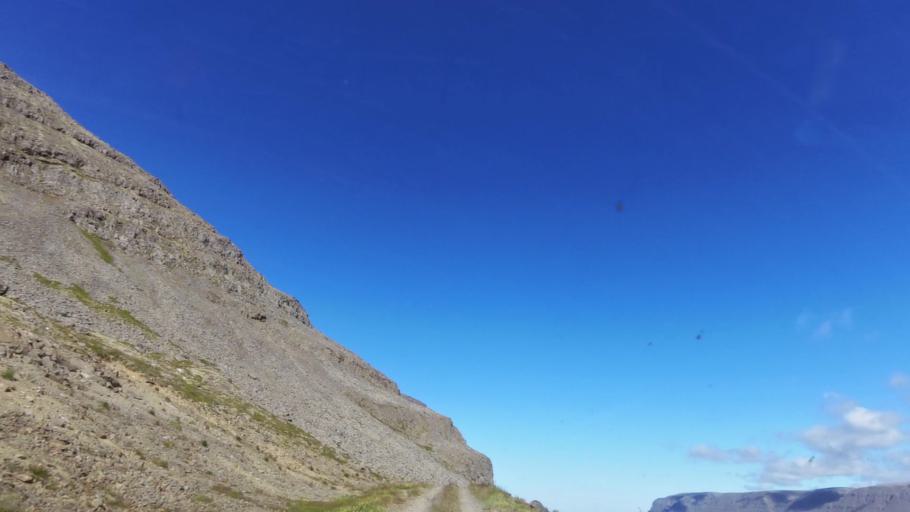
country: IS
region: West
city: Olafsvik
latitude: 65.6226
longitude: -23.8829
